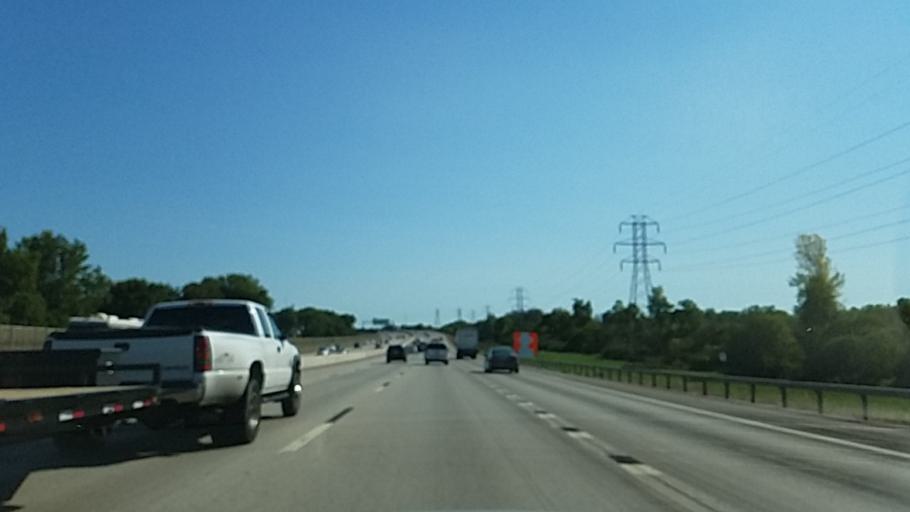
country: US
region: New York
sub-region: Erie County
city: West Seneca
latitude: 42.8625
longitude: -78.7920
